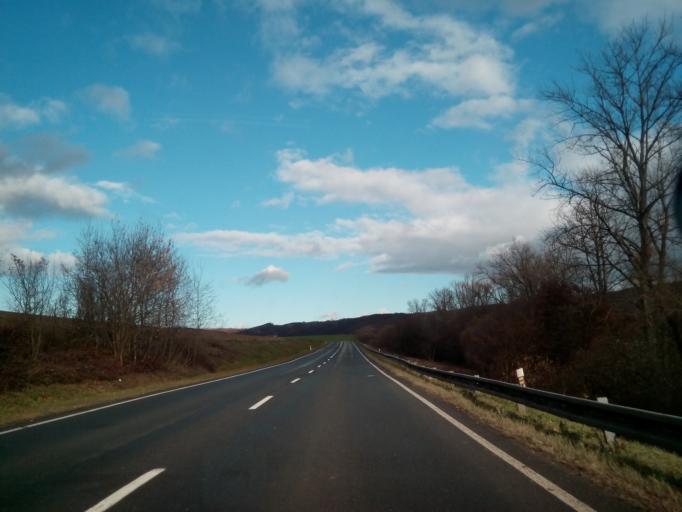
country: SK
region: Presovsky
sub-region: Okres Bardejov
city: Bardejov
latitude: 49.1969
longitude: 21.3092
